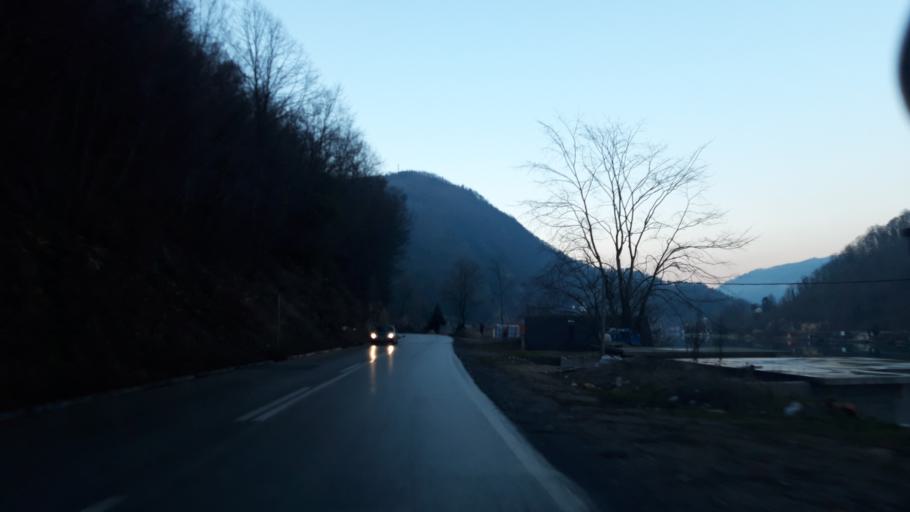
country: RS
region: Central Serbia
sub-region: Macvanski Okrug
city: Mali Zvornik
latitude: 44.3489
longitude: 19.1106
